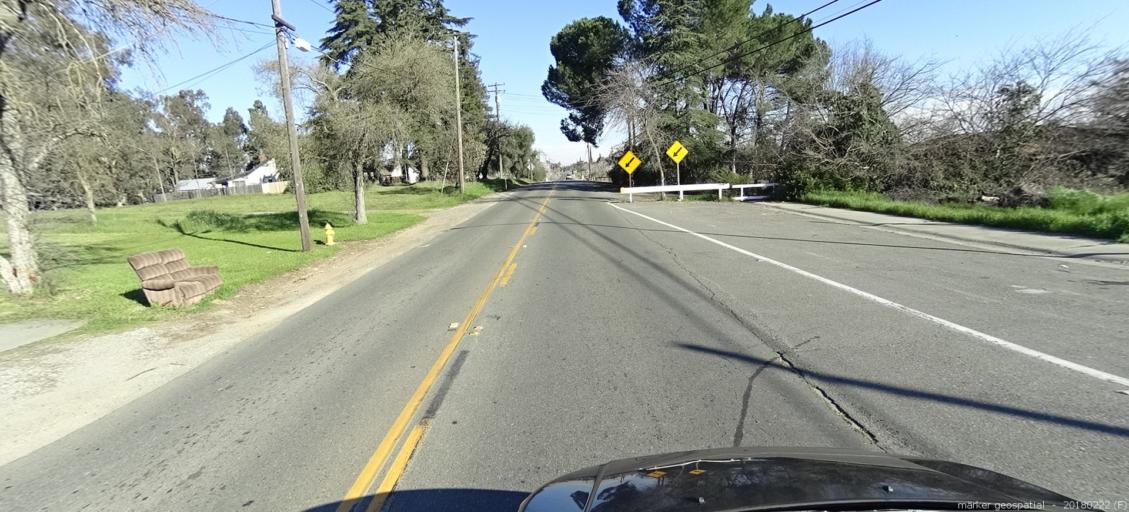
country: US
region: California
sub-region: Sacramento County
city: Elverta
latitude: 38.7153
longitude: -121.4666
